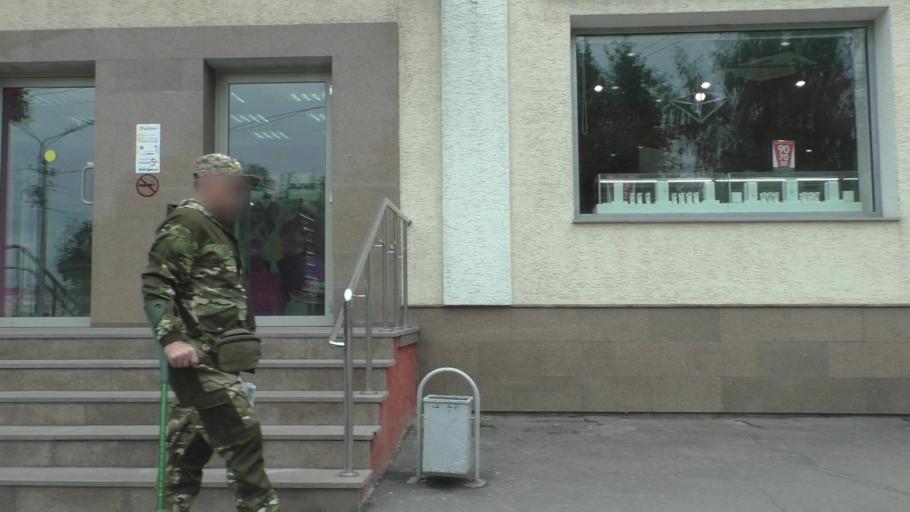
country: RU
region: Moskovskaya
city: Yegor'yevsk
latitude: 55.3805
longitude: 39.0400
